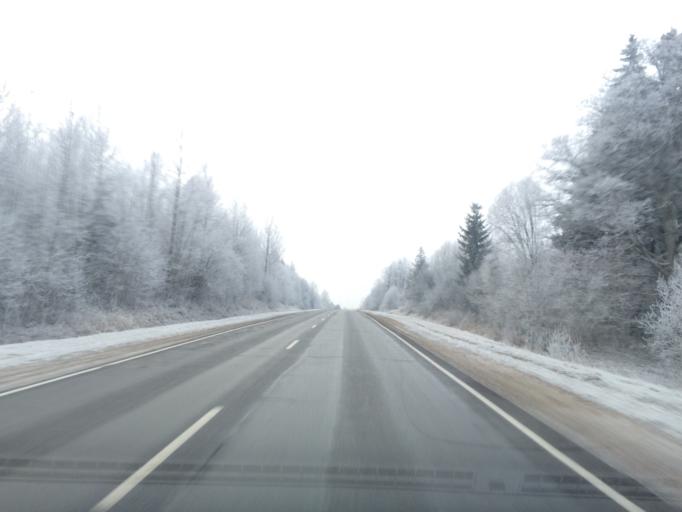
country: LV
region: Rezekne
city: Rezekne
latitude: 56.6197
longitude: 27.4533
